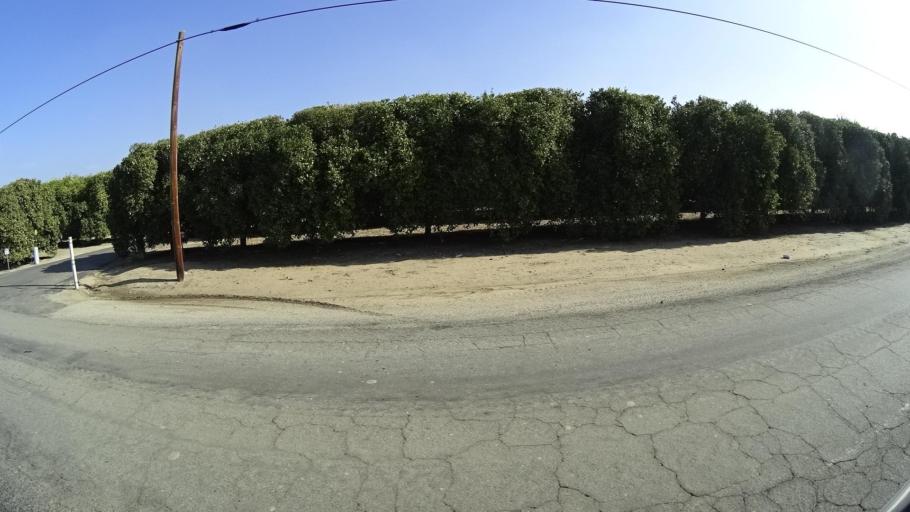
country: US
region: California
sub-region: Kern County
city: McFarland
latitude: 35.6709
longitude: -119.1340
